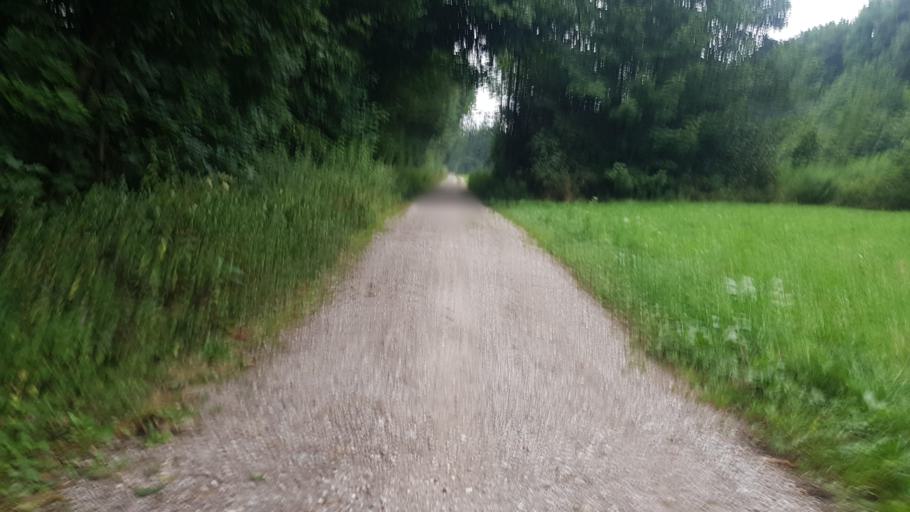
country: DE
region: Bavaria
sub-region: Upper Bavaria
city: Gauting
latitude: 48.0474
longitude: 11.3603
